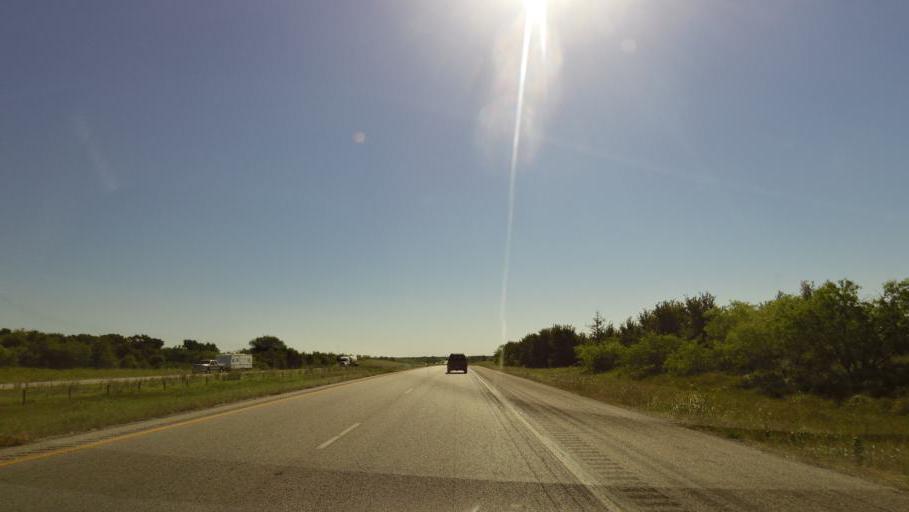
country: US
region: Texas
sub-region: Gonzales County
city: Waelder
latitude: 29.6666
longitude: -97.3327
